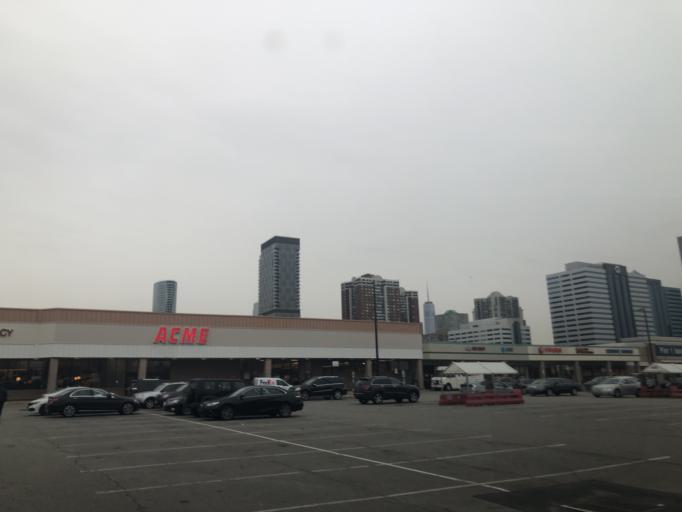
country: US
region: New Jersey
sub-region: Hudson County
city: Hoboken
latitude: 40.7335
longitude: -74.0385
